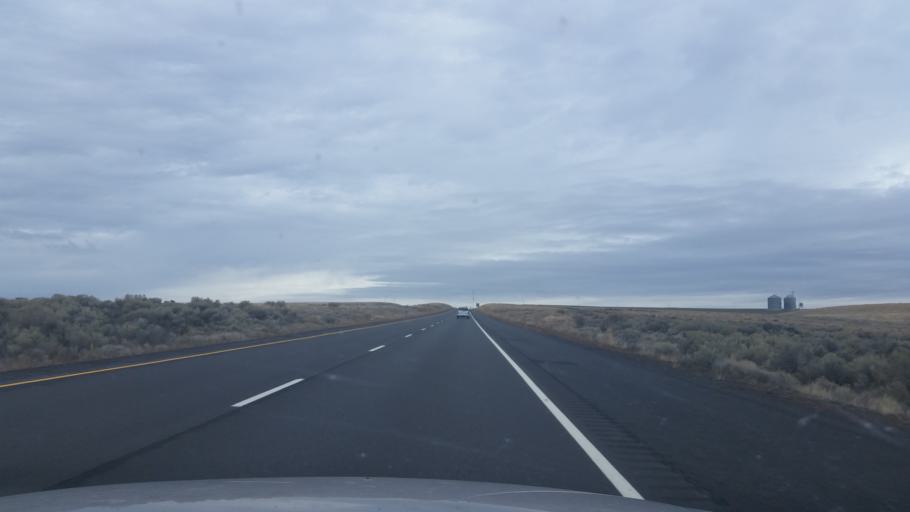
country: US
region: Washington
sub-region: Adams County
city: Ritzville
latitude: 47.0970
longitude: -118.6498
